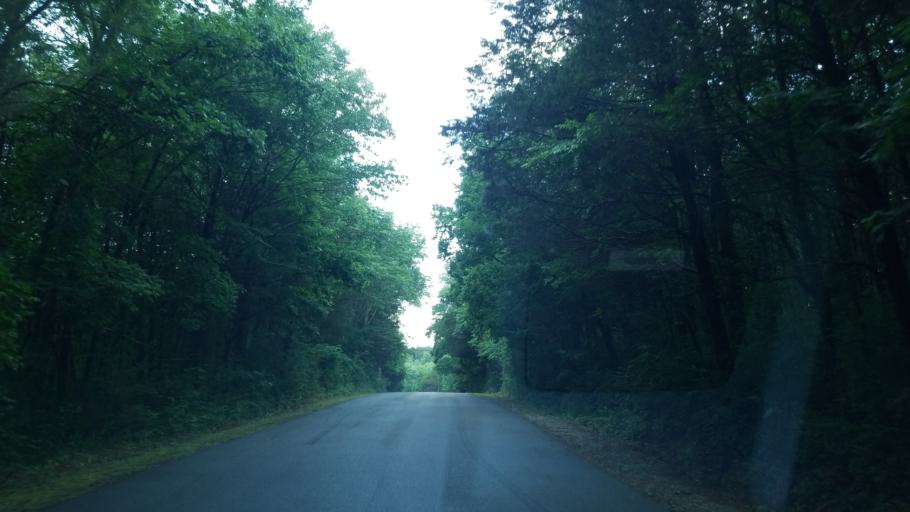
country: US
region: Tennessee
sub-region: Rutherford County
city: La Vergne
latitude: 36.1089
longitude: -86.6212
